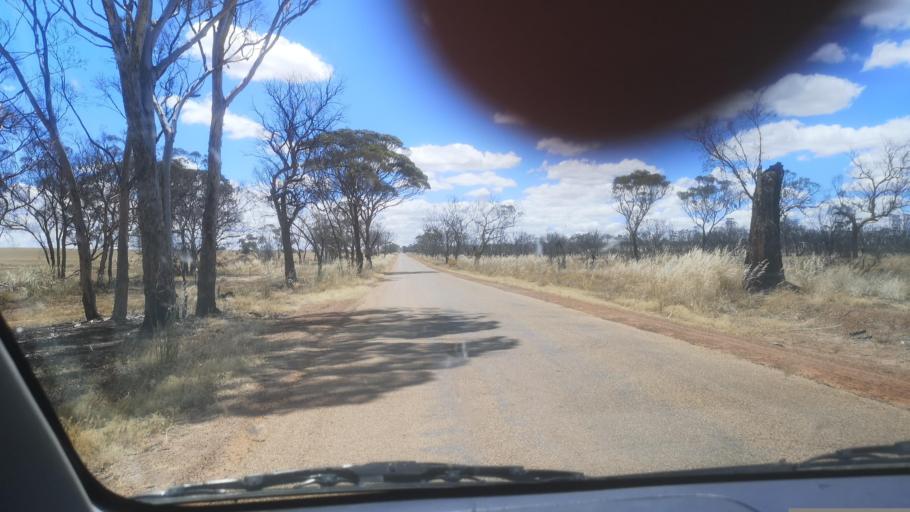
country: AU
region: Western Australia
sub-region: Cunderdin
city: Cunderdin
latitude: -32.1888
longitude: 117.6609
